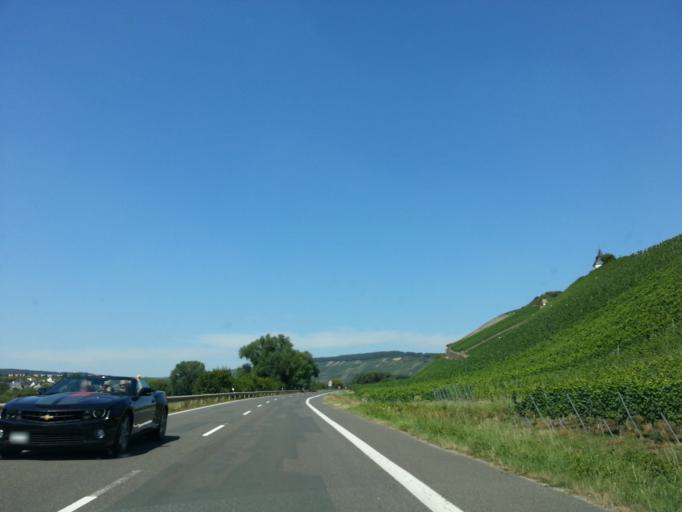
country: DE
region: Rheinland-Pfalz
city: Leiwen
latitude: 49.8203
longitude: 6.8895
